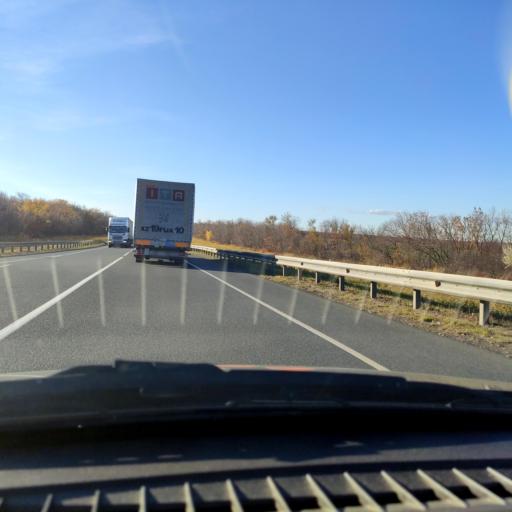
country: RU
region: Samara
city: Mezhdurechensk
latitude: 53.2569
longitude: 49.1205
